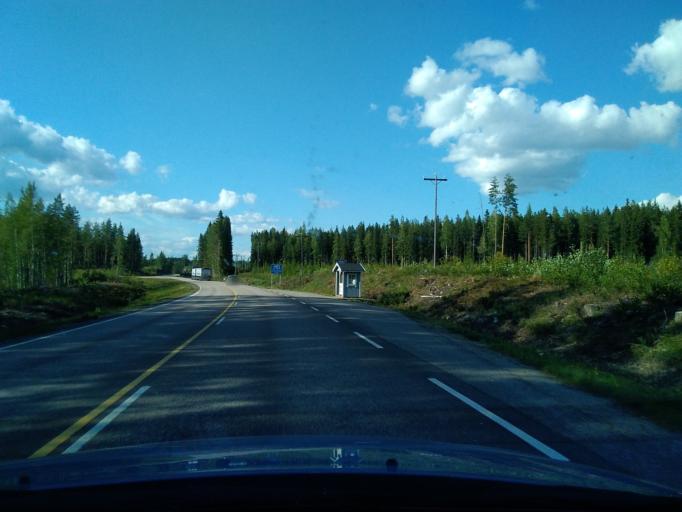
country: FI
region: Pirkanmaa
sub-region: Ylae-Pirkanmaa
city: Maenttae
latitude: 62.1191
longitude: 24.7439
